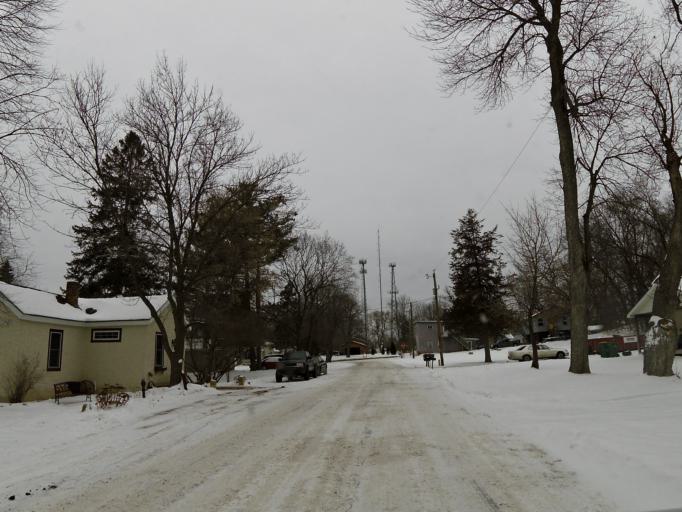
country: US
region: Minnesota
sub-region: Washington County
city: Stillwater
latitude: 45.0587
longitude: -92.7934
